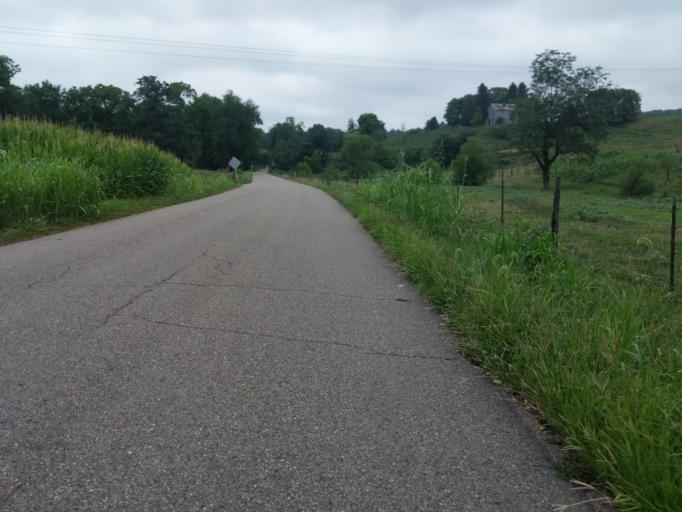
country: US
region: Ohio
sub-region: Athens County
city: Chauncey
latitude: 39.3861
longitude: -82.1439
